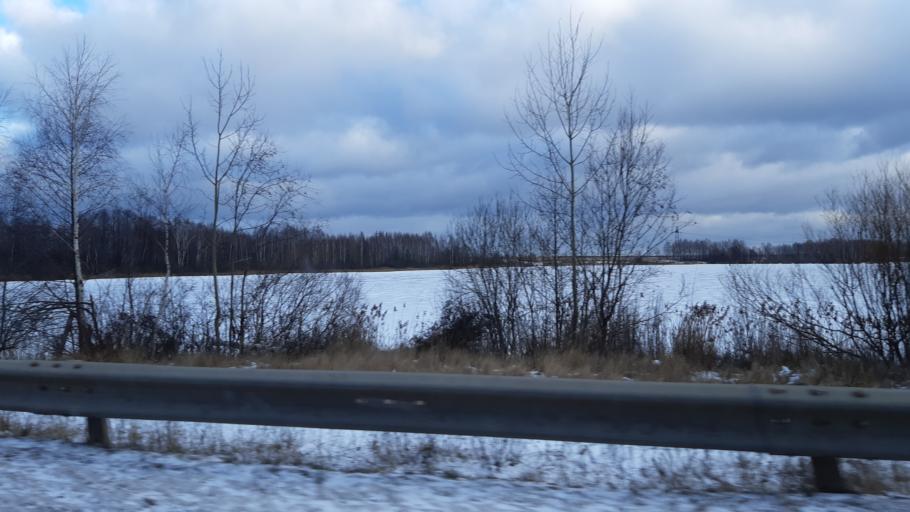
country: RU
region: Moskovskaya
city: Noginsk-9
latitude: 55.9834
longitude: 38.5440
